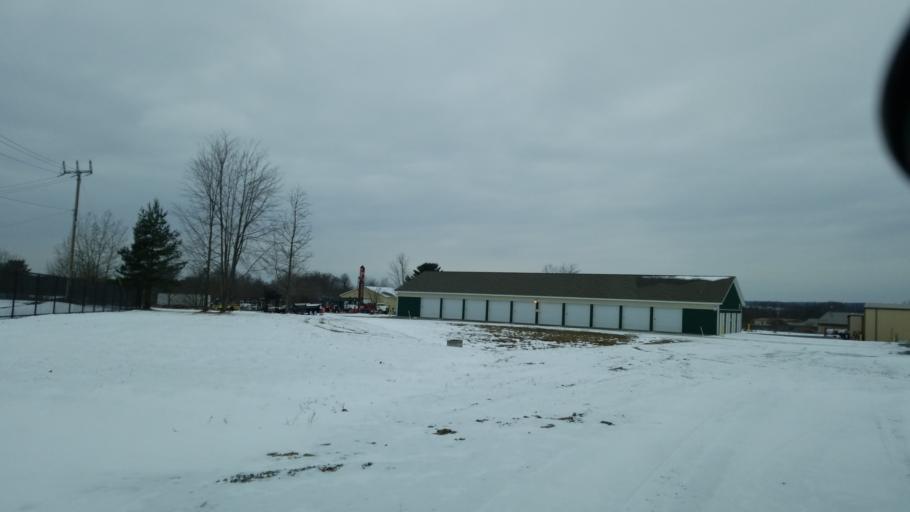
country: US
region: Pennsylvania
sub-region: Clearfield County
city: DuBois
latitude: 41.1074
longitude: -78.7308
